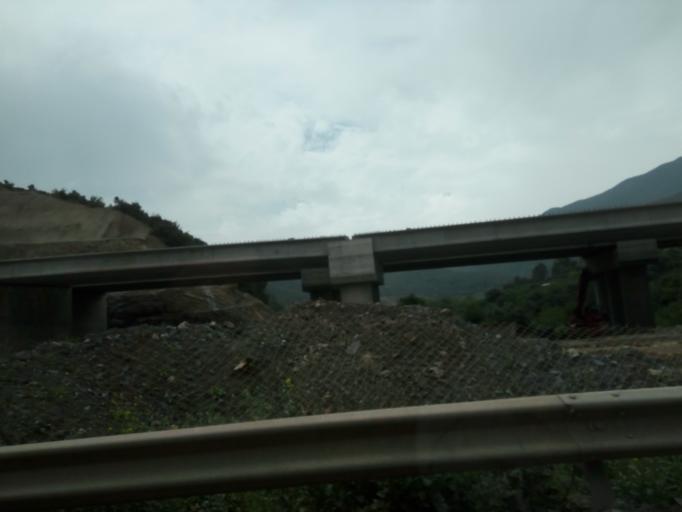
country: DZ
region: Medea
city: Medea
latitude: 36.3330
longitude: 2.7624
